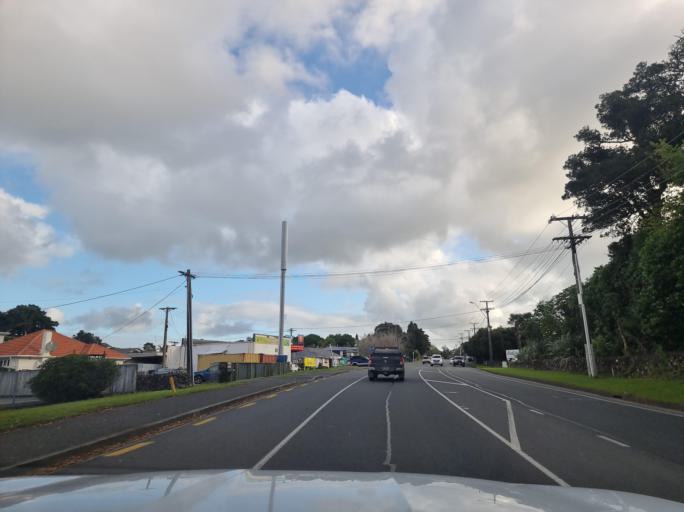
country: NZ
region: Northland
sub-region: Whangarei
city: Whangarei
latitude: -35.7389
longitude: 174.2830
